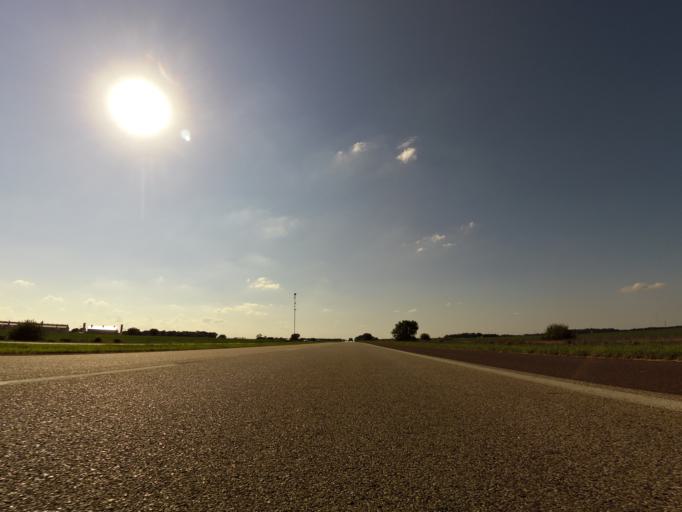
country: US
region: Kansas
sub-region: Reno County
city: Haven
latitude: 37.9074
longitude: -97.8031
